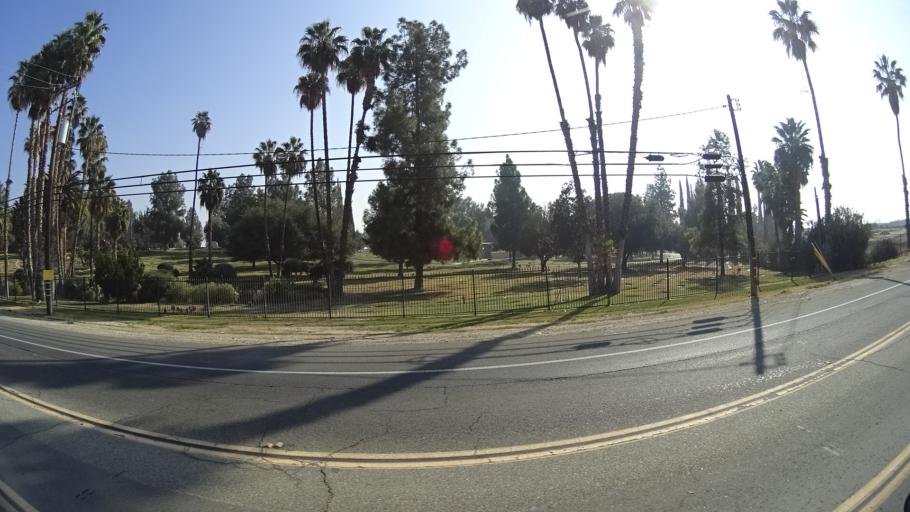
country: US
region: California
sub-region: Kern County
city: Bakersfield
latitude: 35.3794
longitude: -118.9049
